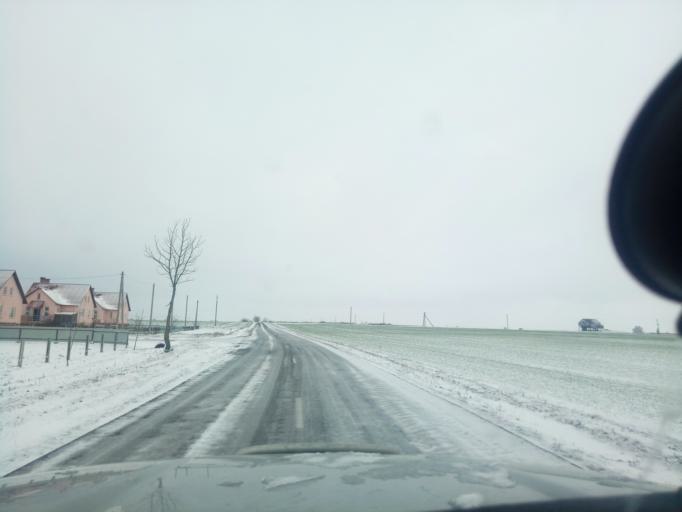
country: BY
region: Minsk
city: Klyetsk
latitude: 53.0512
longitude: 26.7562
